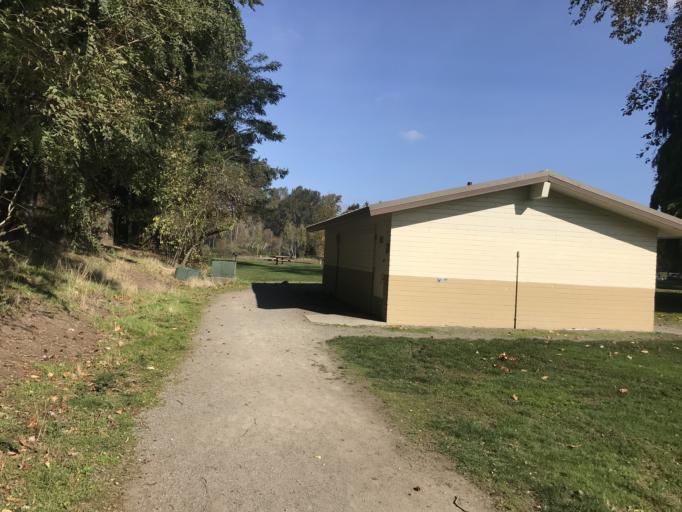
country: US
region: Washington
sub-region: Pierce County
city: University Place
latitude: 47.2475
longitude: -122.5523
